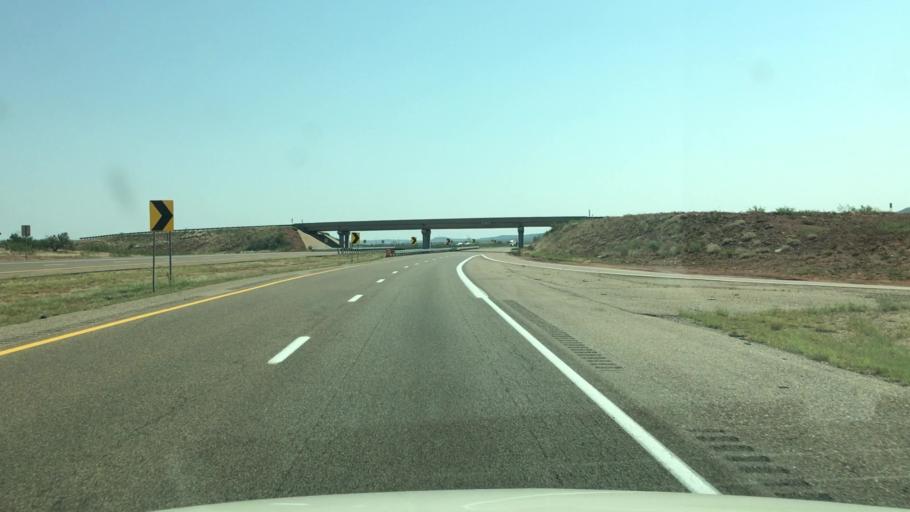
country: US
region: New Mexico
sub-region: Quay County
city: Tucumcari
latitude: 35.0928
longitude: -104.0725
